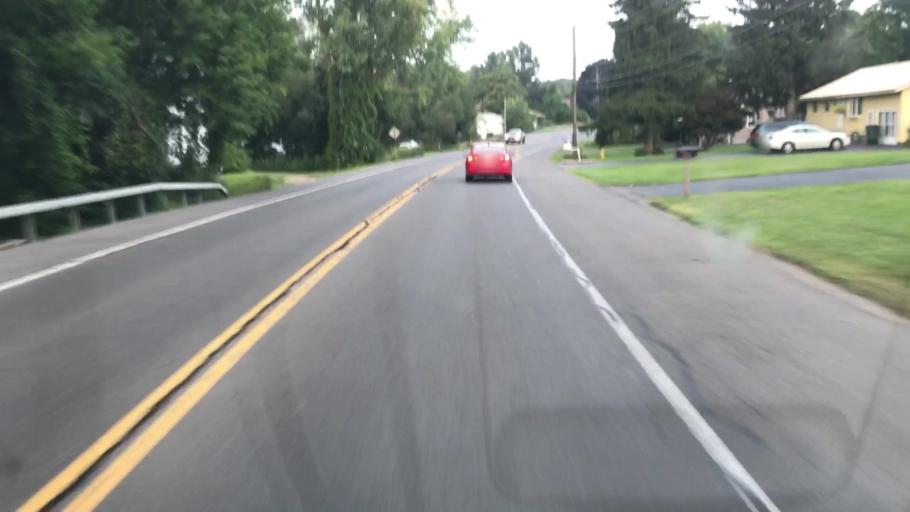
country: US
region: New York
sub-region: Onondaga County
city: North Syracuse
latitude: 43.1422
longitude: -76.1499
